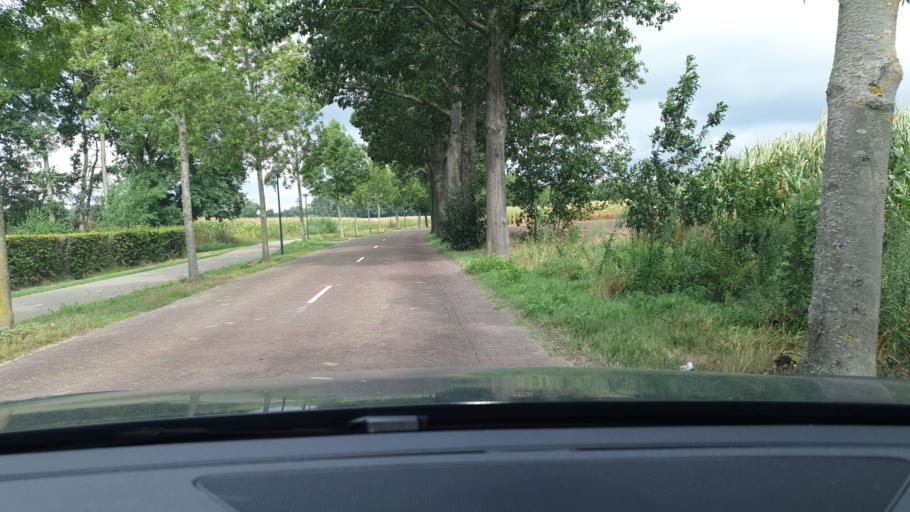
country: NL
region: North Brabant
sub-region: Gemeente Son en Breugel
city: Breugel
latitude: 51.5021
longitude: 5.5106
